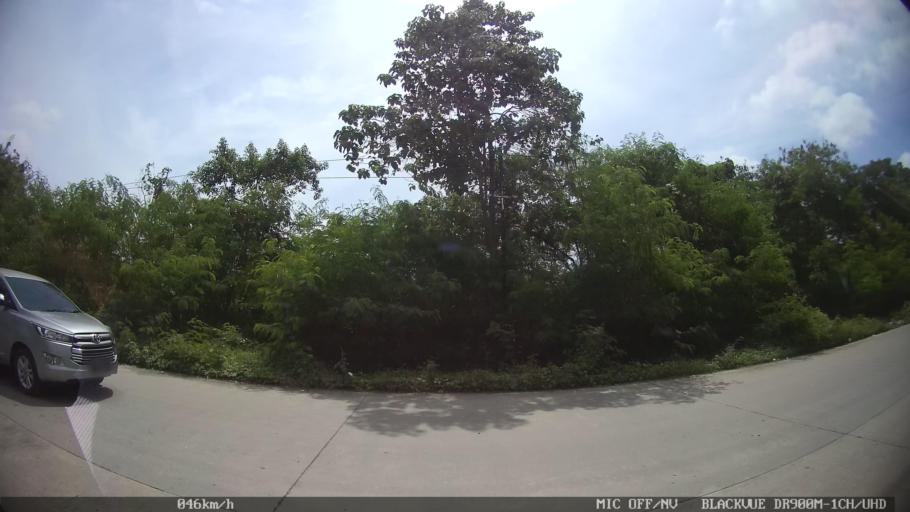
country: ID
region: North Sumatra
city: Medan
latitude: 3.6407
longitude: 98.7084
